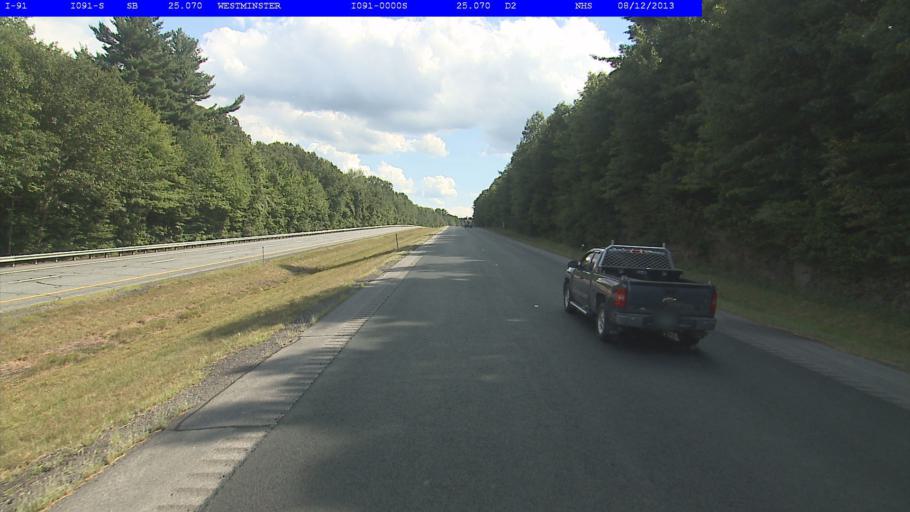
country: US
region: New Hampshire
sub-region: Cheshire County
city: Westmoreland
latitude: 43.0421
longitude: -72.4696
